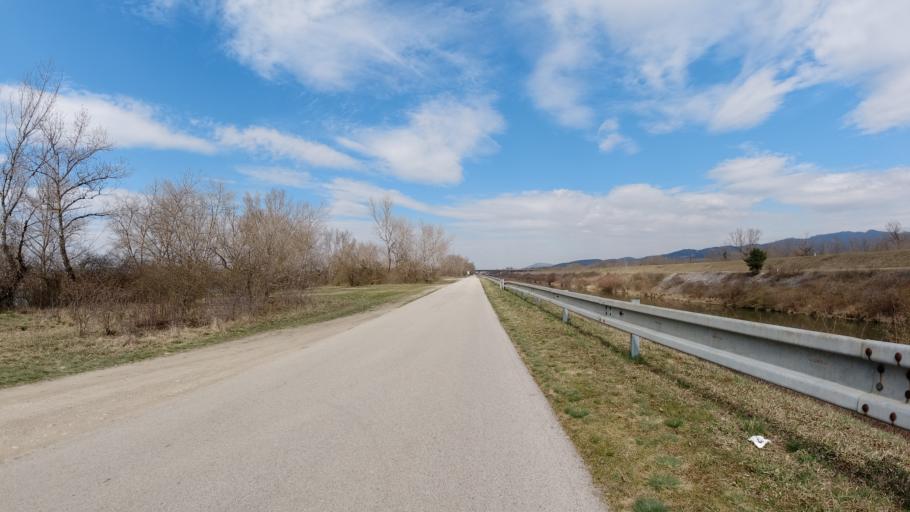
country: SK
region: Trnavsky
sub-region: Okres Trnava
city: Piestany
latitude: 48.6417
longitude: 17.8466
